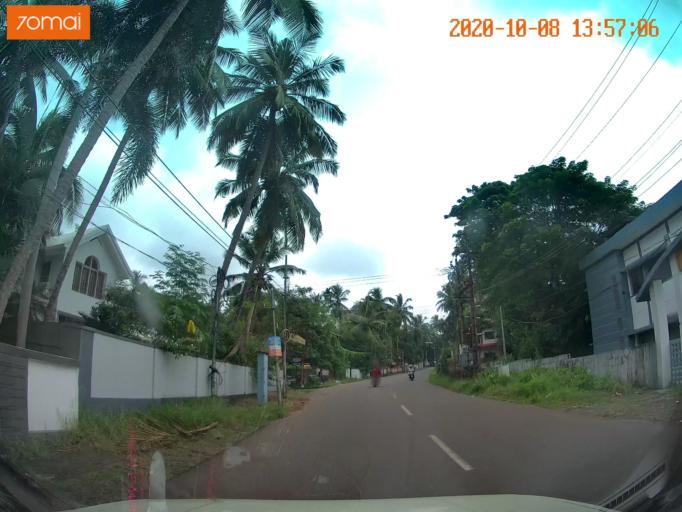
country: IN
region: Kerala
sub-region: Kozhikode
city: Kozhikode
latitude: 11.2900
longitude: 75.8013
